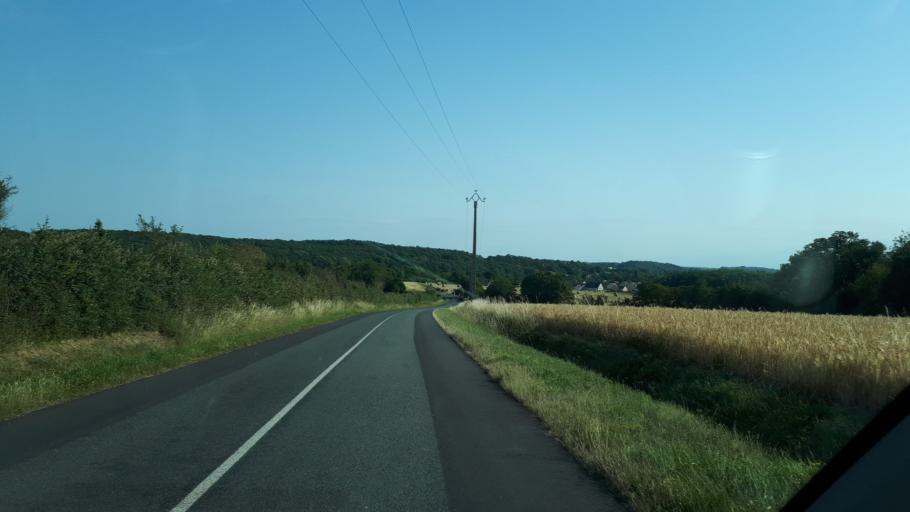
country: FR
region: Centre
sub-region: Departement du Loir-et-Cher
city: Aze
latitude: 47.8615
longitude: 1.0041
